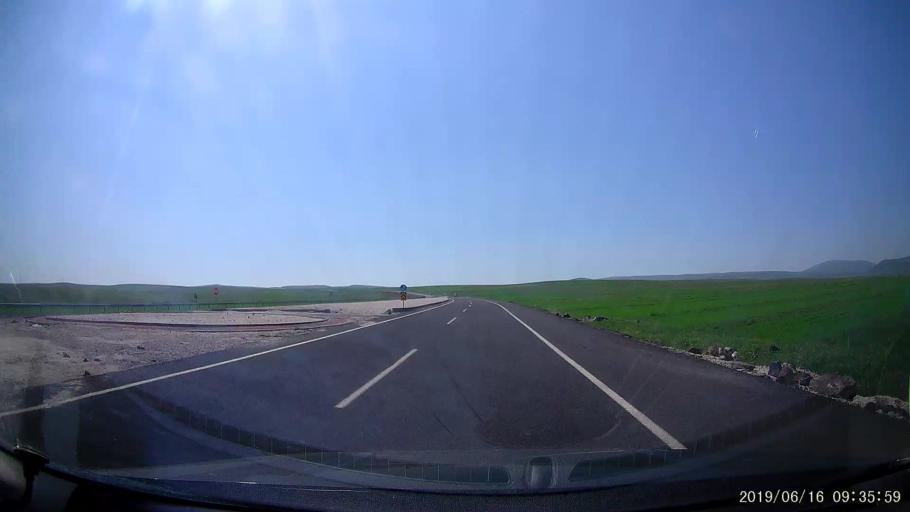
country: TR
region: Kars
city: Kars
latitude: 40.5633
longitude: 43.1648
